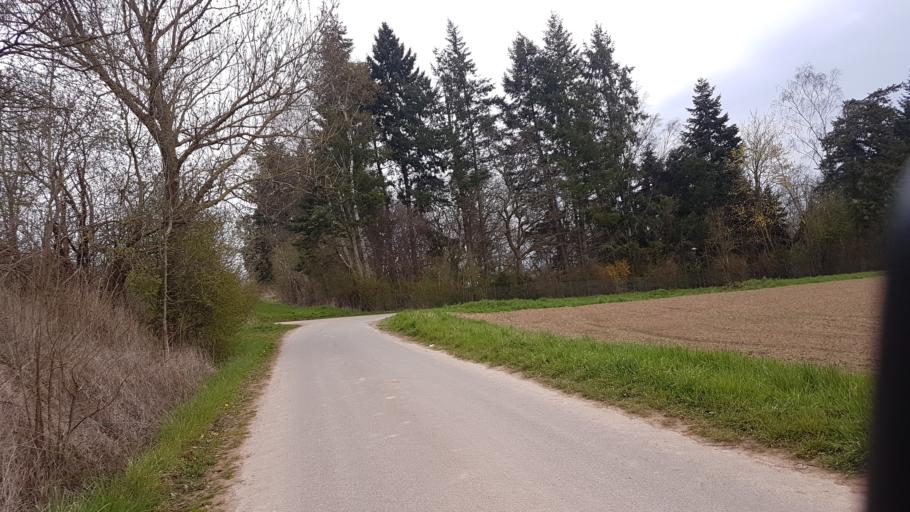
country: DE
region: Lower Saxony
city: Hameln
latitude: 52.1272
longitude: 9.3236
